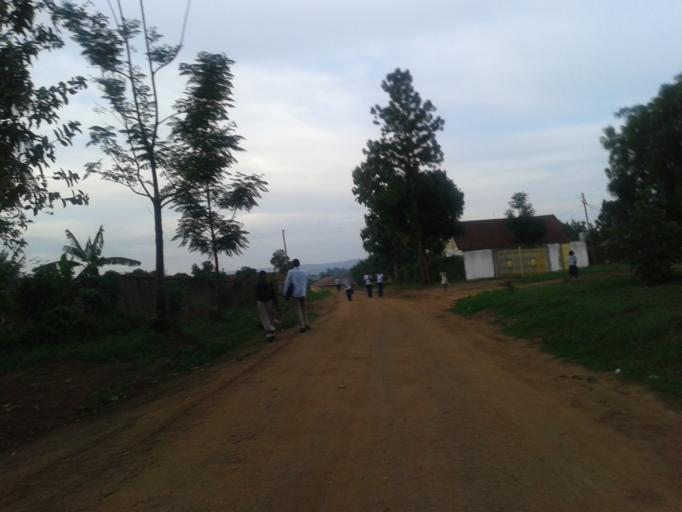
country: UG
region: Eastern Region
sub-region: Mbale District
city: Mbale
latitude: 1.0810
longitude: 34.1765
